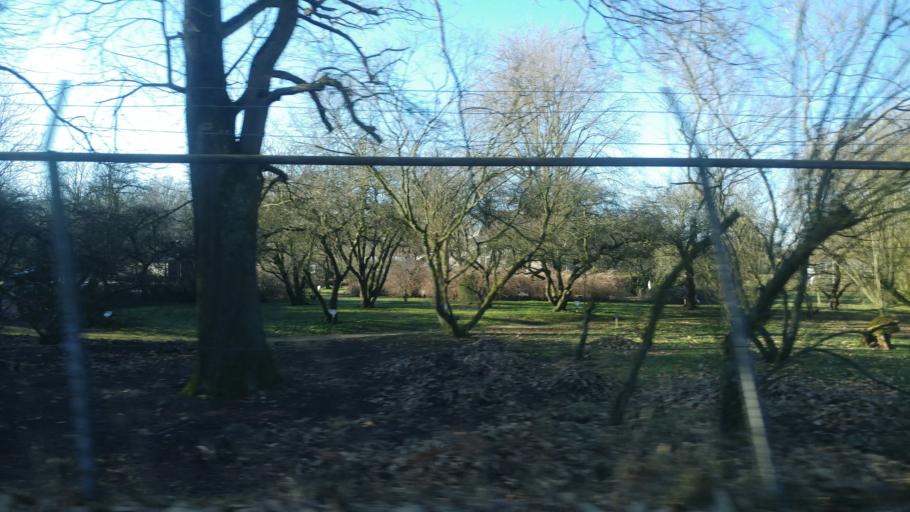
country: NL
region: North Brabant
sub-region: Gemeente Tilburg
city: Tilburg
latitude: 51.5296
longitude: 5.1214
